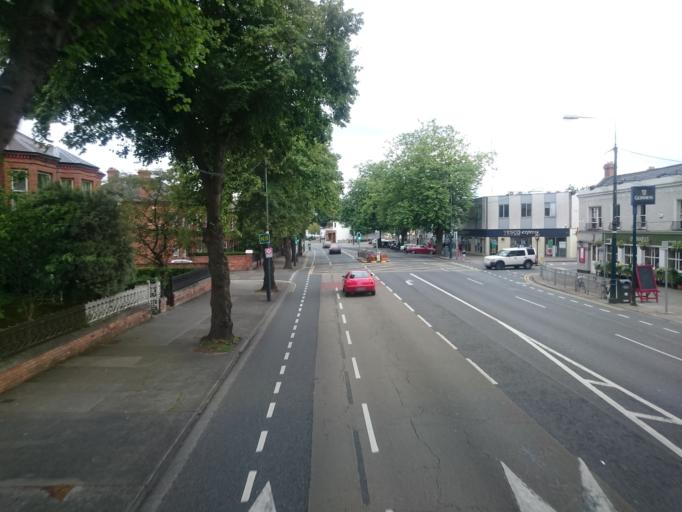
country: IE
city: Clonskeagh
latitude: 53.3232
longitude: -6.2384
